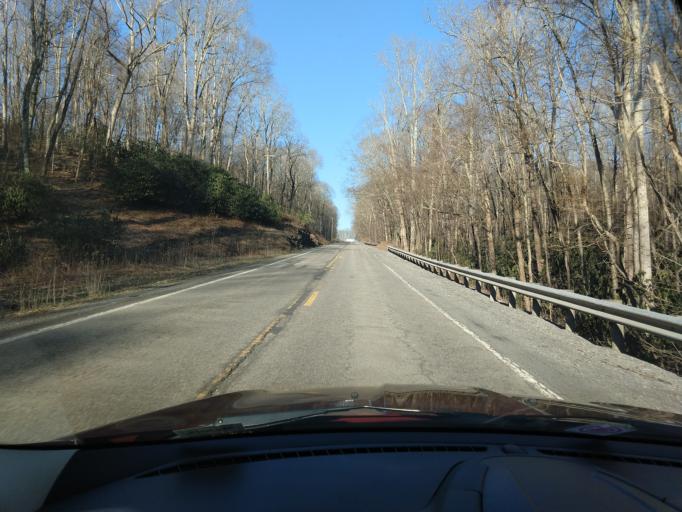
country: US
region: West Virginia
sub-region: Fayette County
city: Fayetteville
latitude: 38.0496
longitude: -80.9506
